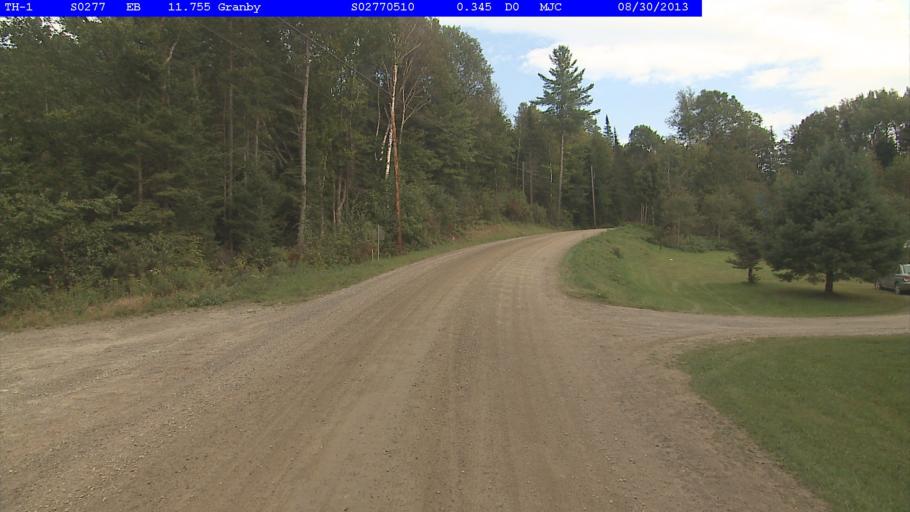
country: US
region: Vermont
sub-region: Essex County
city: Guildhall
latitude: 44.5707
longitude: -71.7548
